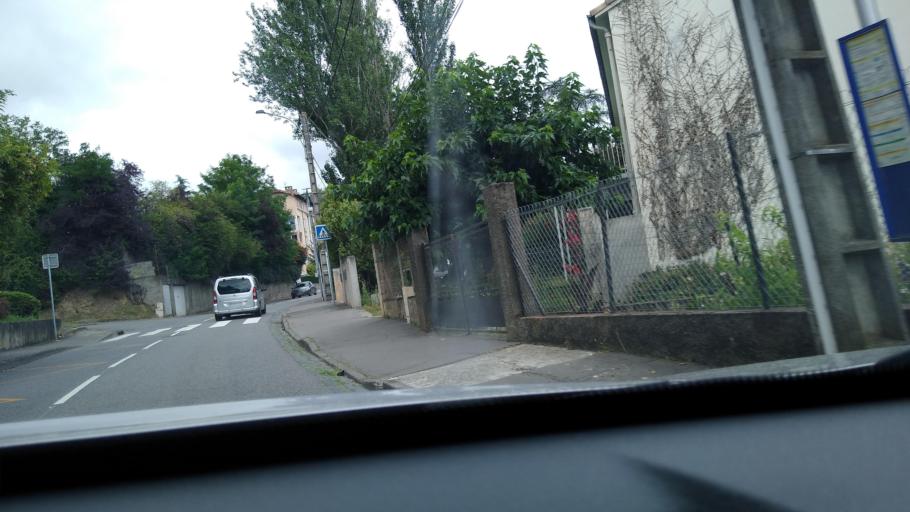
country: FR
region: Midi-Pyrenees
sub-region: Departement de la Haute-Garonne
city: Balma
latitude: 43.6054
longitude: 1.4764
